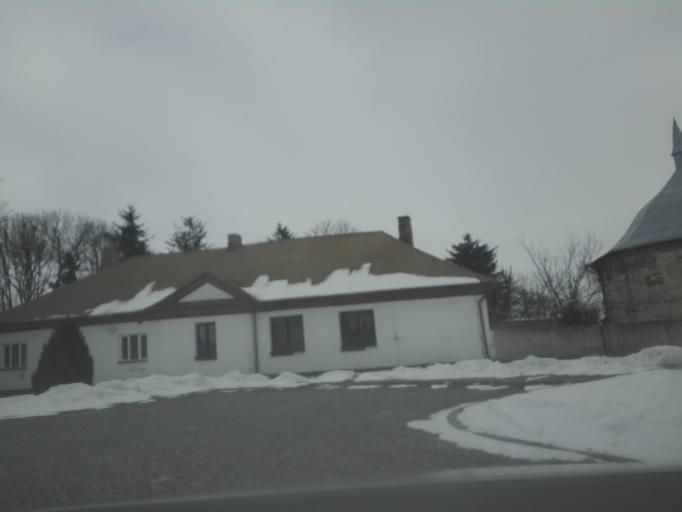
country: PL
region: Lublin Voivodeship
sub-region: Powiat hrubieszowski
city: Horodlo
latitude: 50.8408
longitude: 24.0321
